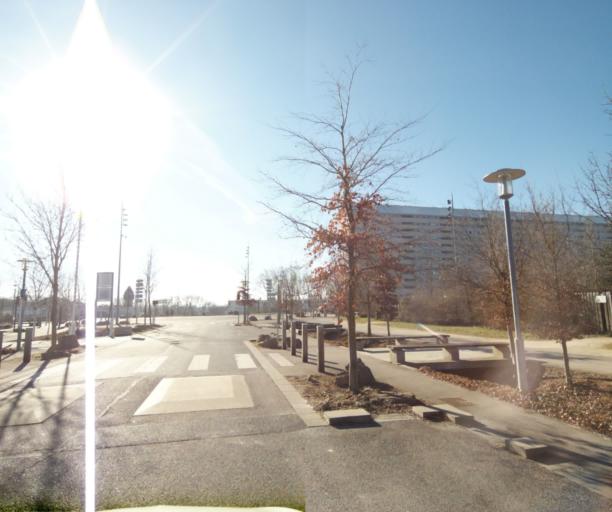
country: FR
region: Lorraine
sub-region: Departement de Meurthe-et-Moselle
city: Maxeville
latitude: 48.7026
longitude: 6.1513
